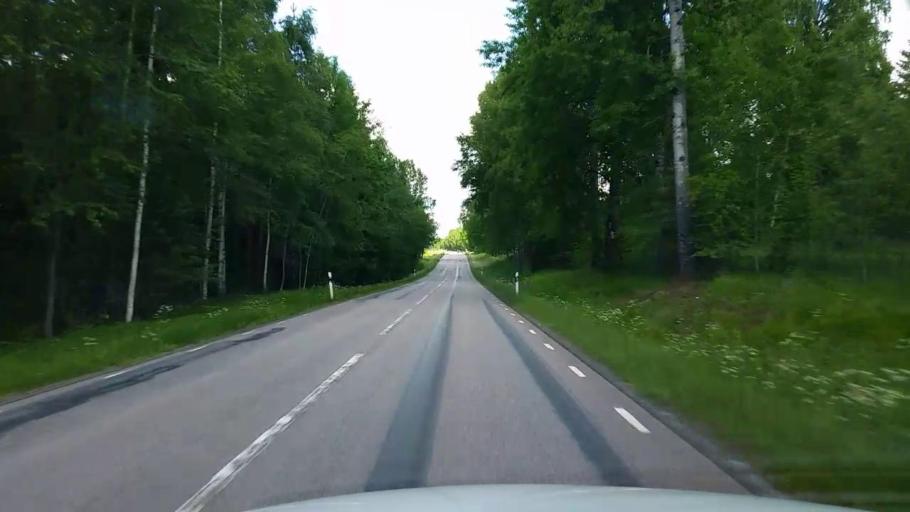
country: SE
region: Vaestmanland
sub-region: Kopings Kommun
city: Kolsva
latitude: 59.6742
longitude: 15.7690
